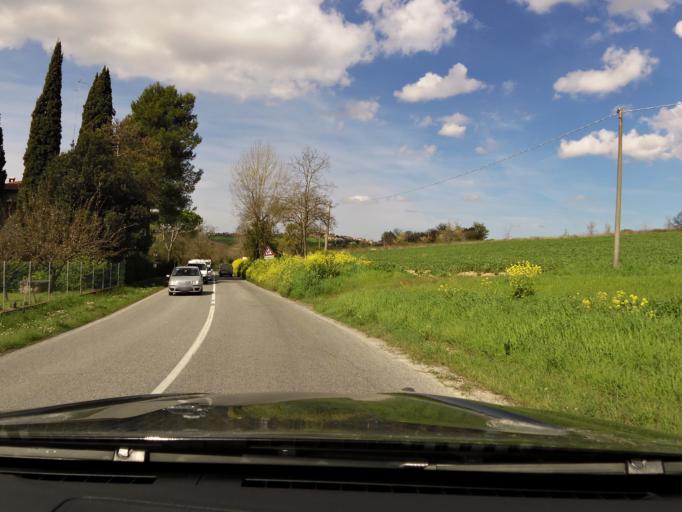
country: IT
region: The Marches
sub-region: Provincia di Ancona
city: Castelfidardo
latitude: 43.4789
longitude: 13.5572
